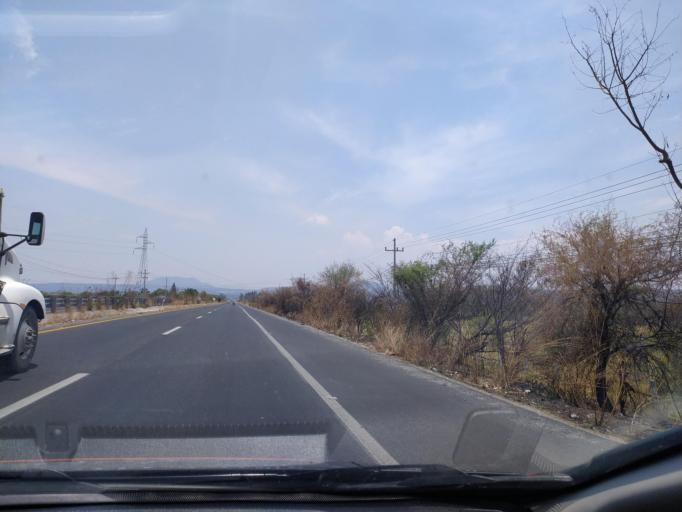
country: MX
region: Jalisco
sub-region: Acatlan de Juarez
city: Villa de los Ninos
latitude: 20.3799
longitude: -103.5928
